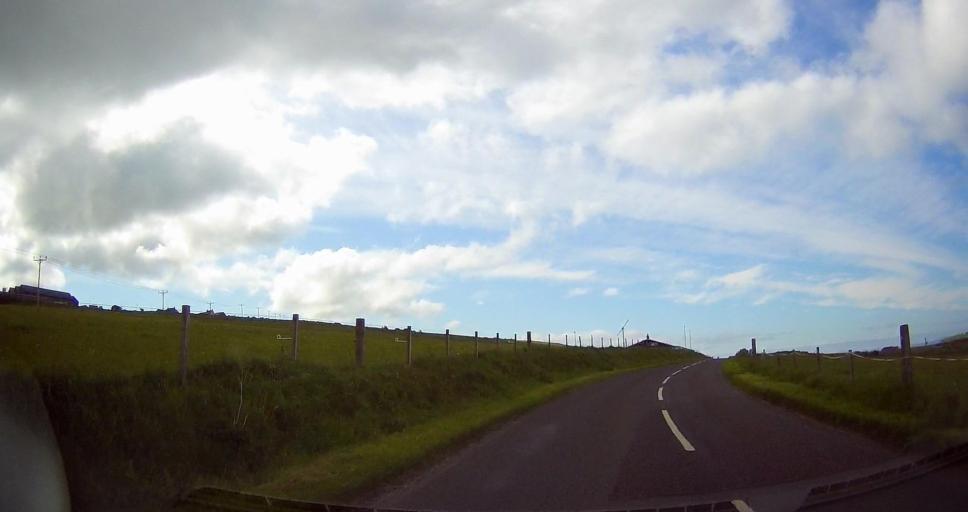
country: GB
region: Scotland
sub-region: Orkney Islands
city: Orkney
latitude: 58.9714
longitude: -2.9614
